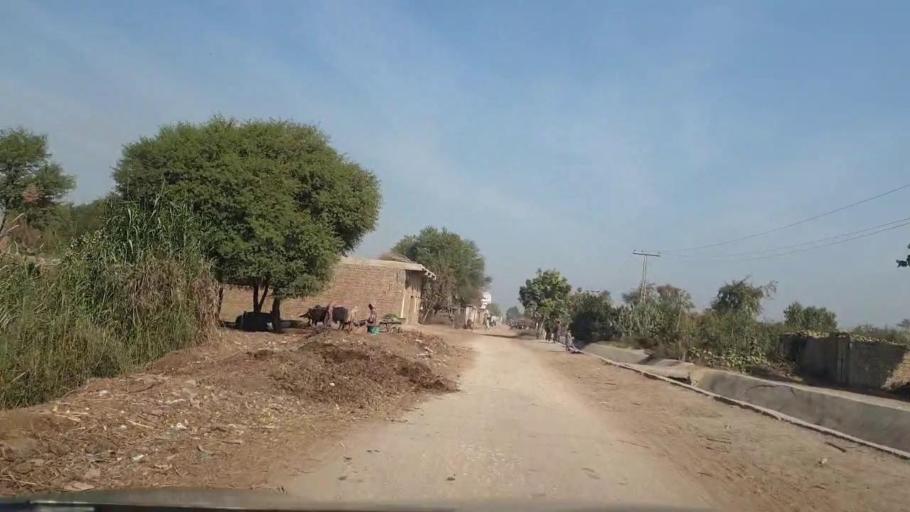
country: PK
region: Sindh
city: Tando Allahyar
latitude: 25.5998
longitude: 68.7222
